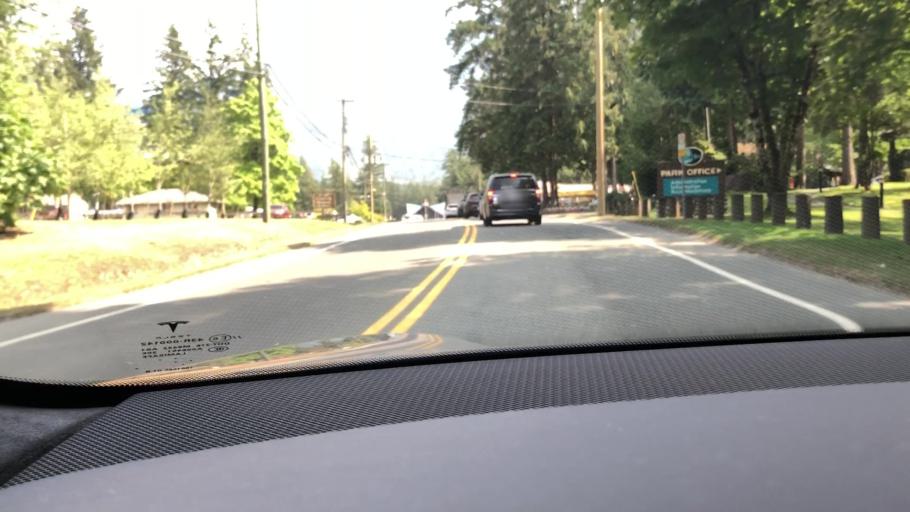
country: CA
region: British Columbia
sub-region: Fraser Valley Regional District
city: Chilliwack
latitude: 49.0766
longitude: -121.9786
